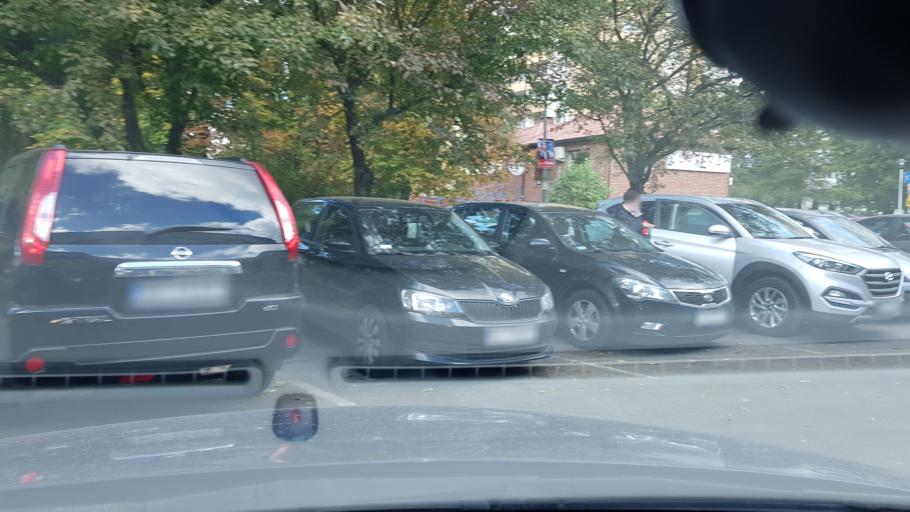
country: PL
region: Masovian Voivodeship
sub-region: Warszawa
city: Bielany
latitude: 52.2738
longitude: 20.9306
